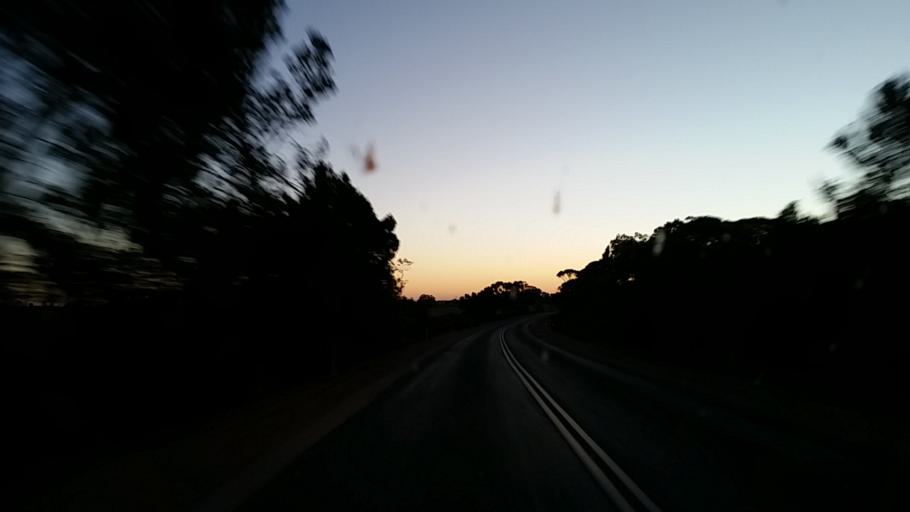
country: AU
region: South Australia
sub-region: Wakefield
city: Balaklava
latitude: -34.1085
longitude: 138.4904
